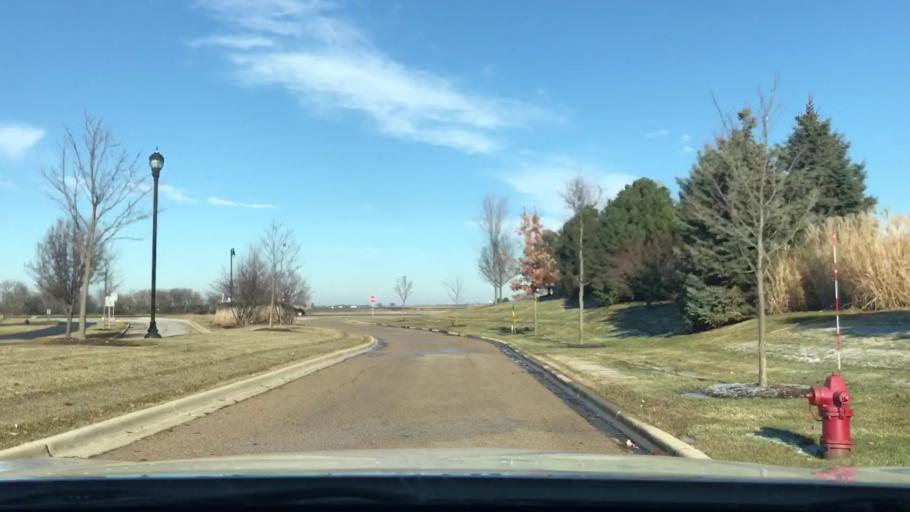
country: US
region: Illinois
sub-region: Kane County
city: Pingree Grove
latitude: 42.0876
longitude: -88.4510
